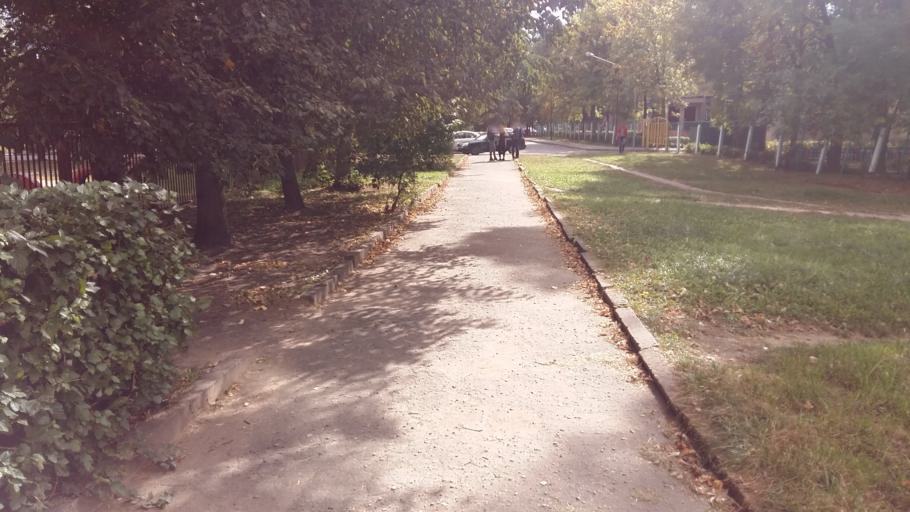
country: BY
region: Grodnenskaya
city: Hrodna
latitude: 53.6921
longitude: 23.8047
